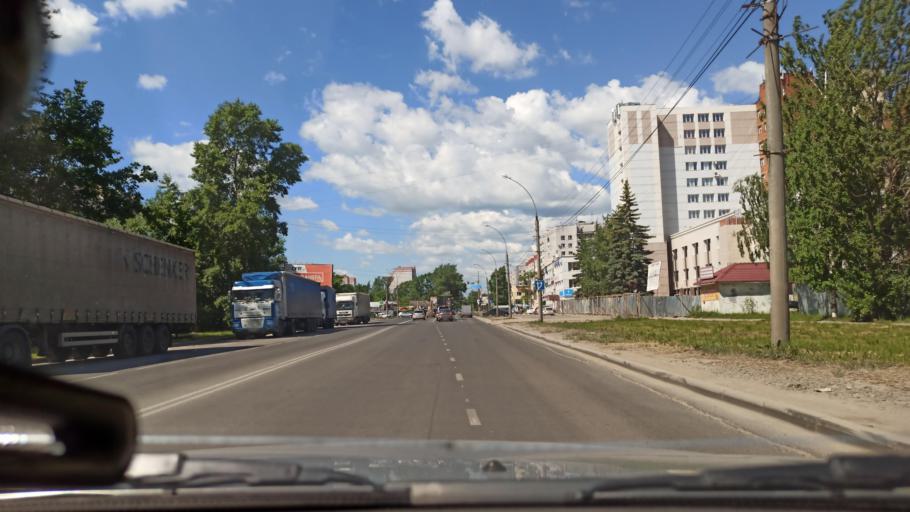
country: RU
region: Vologda
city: Vologda
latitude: 59.2109
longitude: 39.8546
